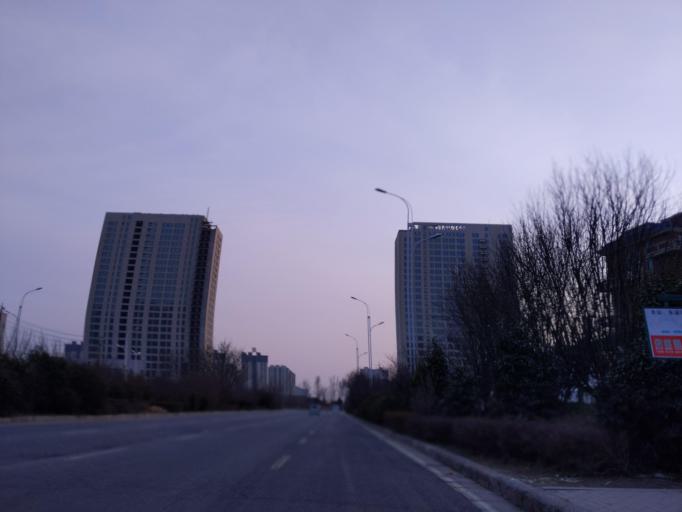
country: CN
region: Henan Sheng
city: Zhongyuanlu
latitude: 35.7818
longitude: 115.1270
